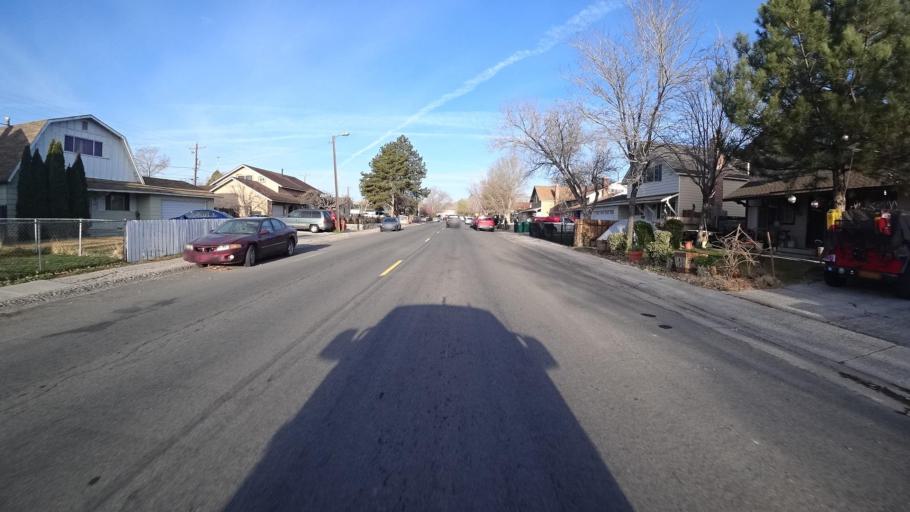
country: US
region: Nevada
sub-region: Washoe County
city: Sparks
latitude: 39.5386
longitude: -119.7828
